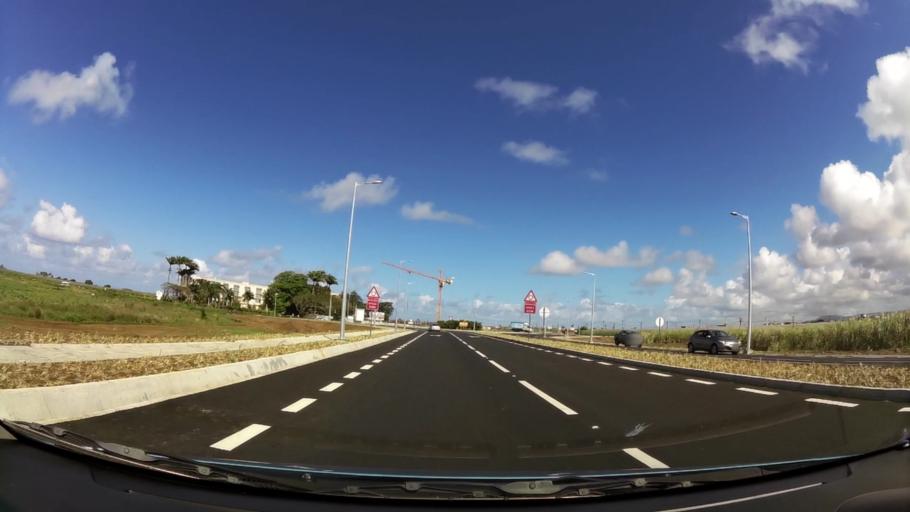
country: MU
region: Grand Port
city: Plaine Magnien
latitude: -20.4381
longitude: 57.6718
